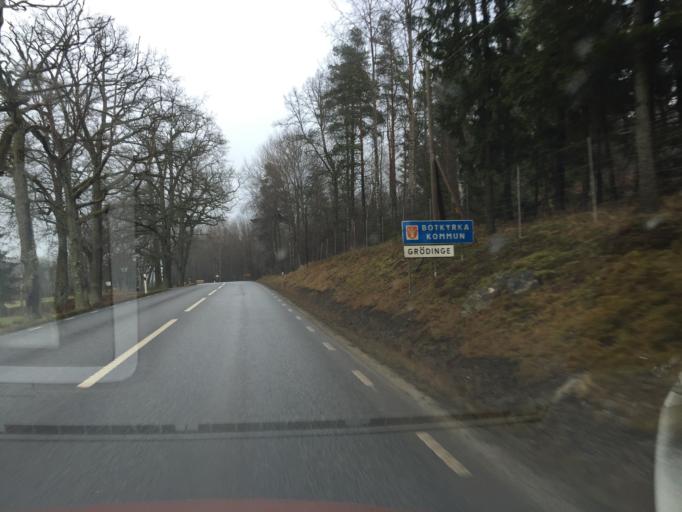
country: SE
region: Stockholm
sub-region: Salems Kommun
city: Ronninge
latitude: 59.1641
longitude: 17.7389
